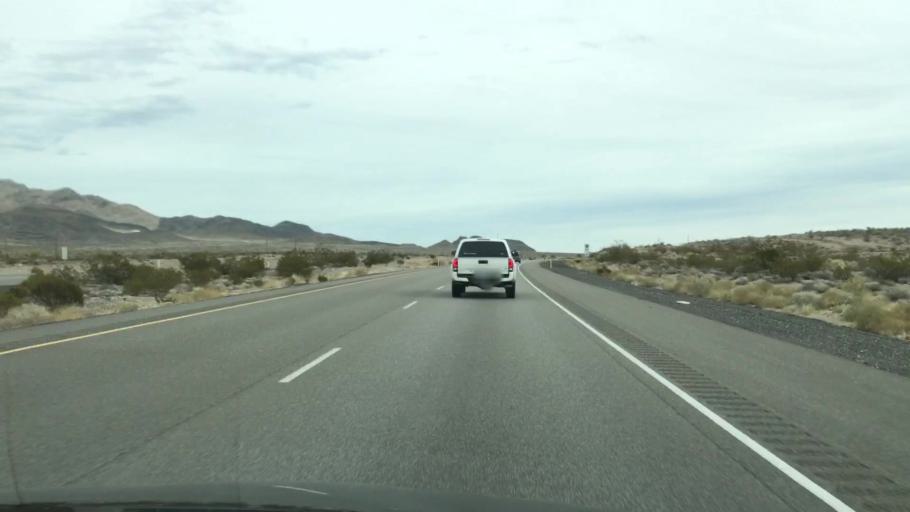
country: US
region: Nevada
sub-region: Nye County
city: Pahrump
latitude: 36.6012
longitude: -115.9802
